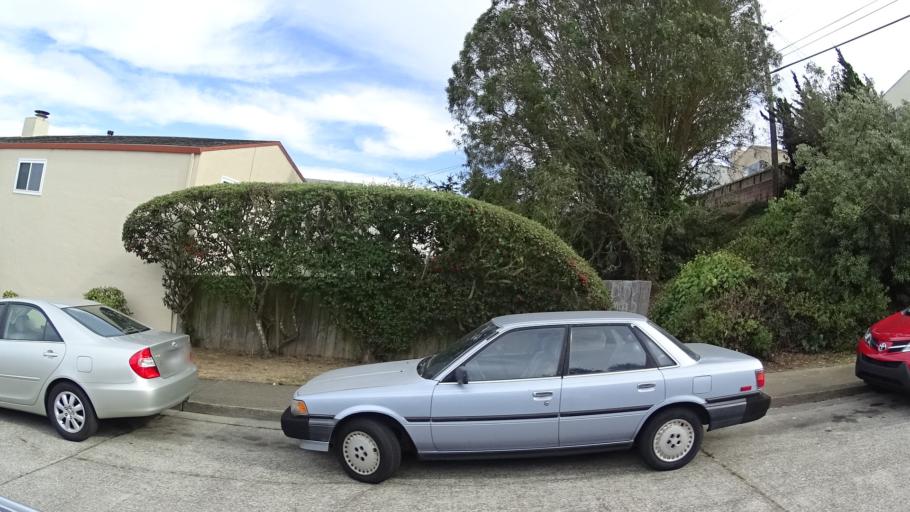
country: US
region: California
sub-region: San Mateo County
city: Daly City
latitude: 37.7082
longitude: -122.4389
